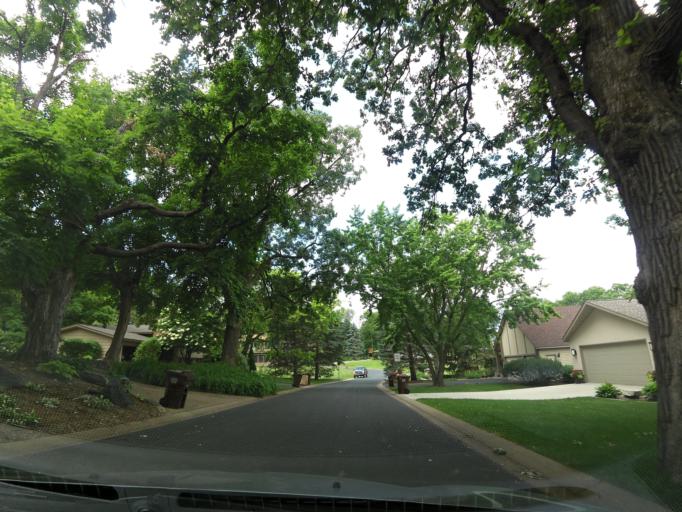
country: US
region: Minnesota
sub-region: Scott County
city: Prior Lake
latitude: 44.7070
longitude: -93.4481
